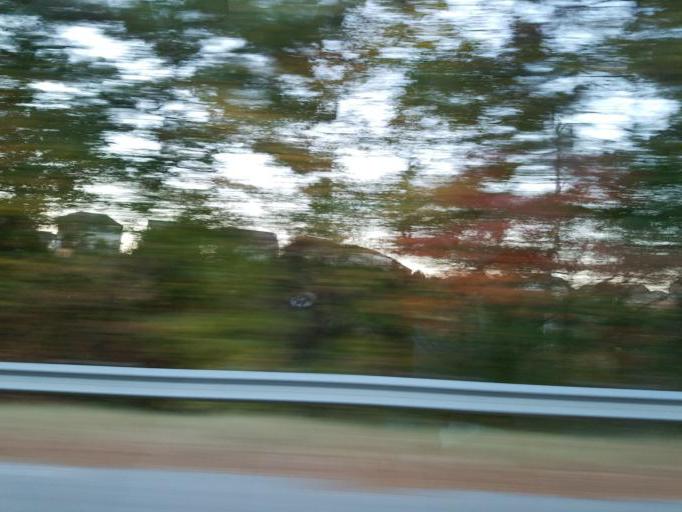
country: US
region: Georgia
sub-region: Forsyth County
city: Cumming
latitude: 34.2593
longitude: -84.0904
